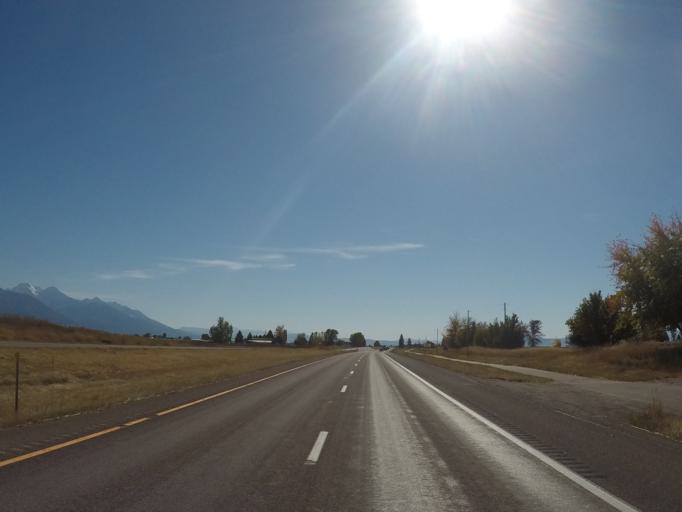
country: US
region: Montana
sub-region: Lake County
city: Pablo
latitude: 47.5735
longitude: -114.1133
